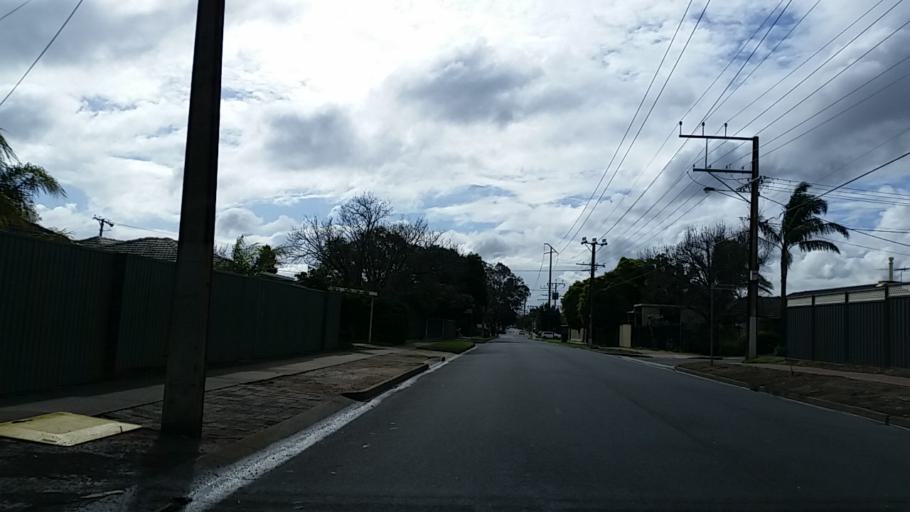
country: AU
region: South Australia
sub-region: Campbelltown
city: Campbelltown
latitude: -34.8905
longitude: 138.6813
